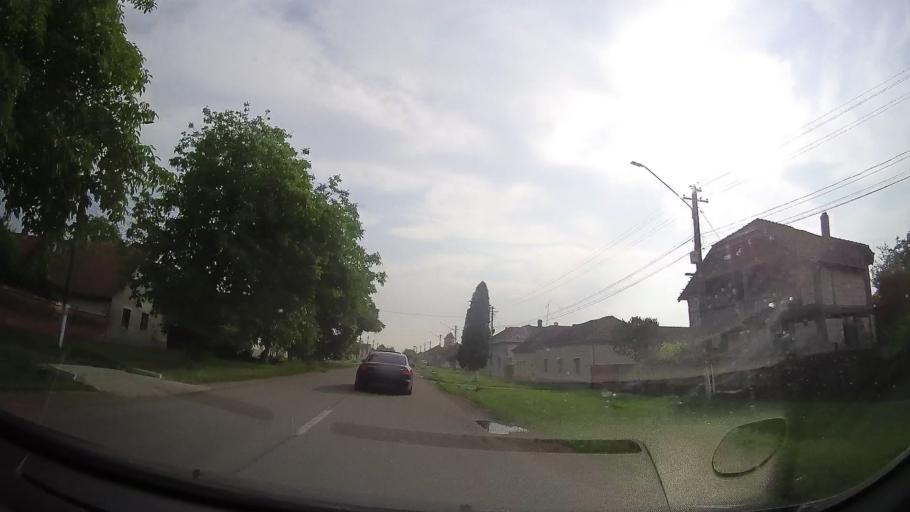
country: RO
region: Timis
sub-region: Comuna Peciu Nou
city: Peciu Nou
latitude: 45.6044
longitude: 21.0553
